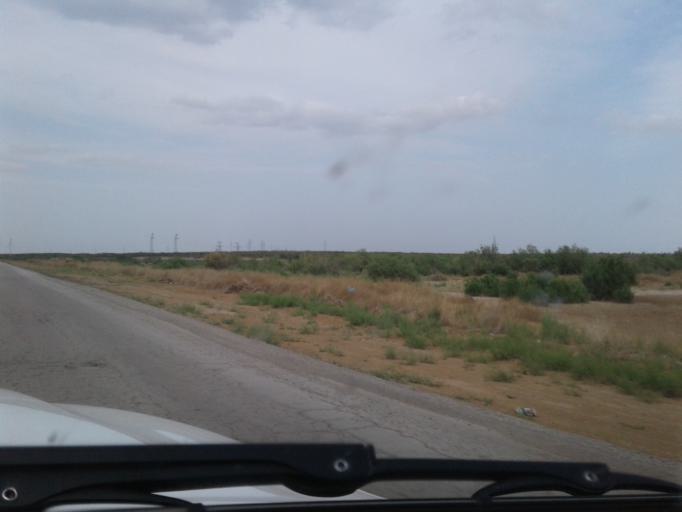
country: TM
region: Mary
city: Mary
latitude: 37.3339
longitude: 61.4210
